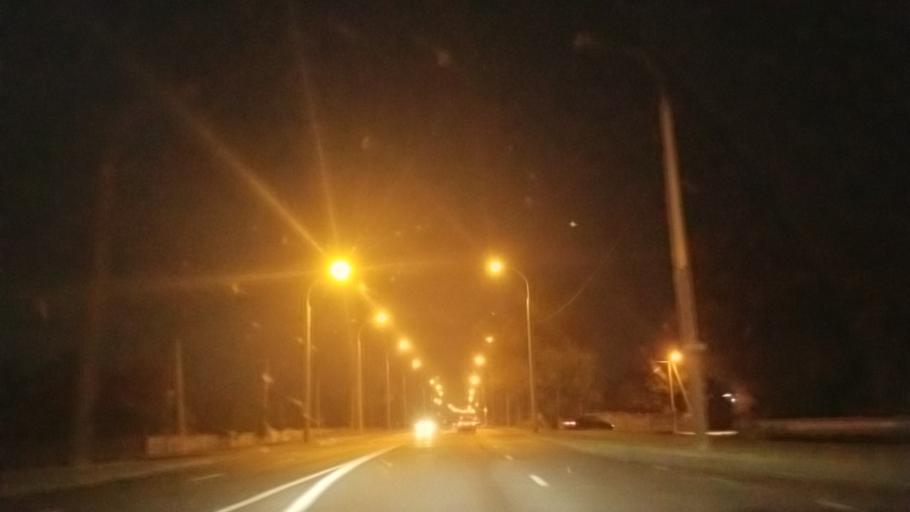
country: BY
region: Brest
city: Brest
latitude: 52.0635
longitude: 23.7359
